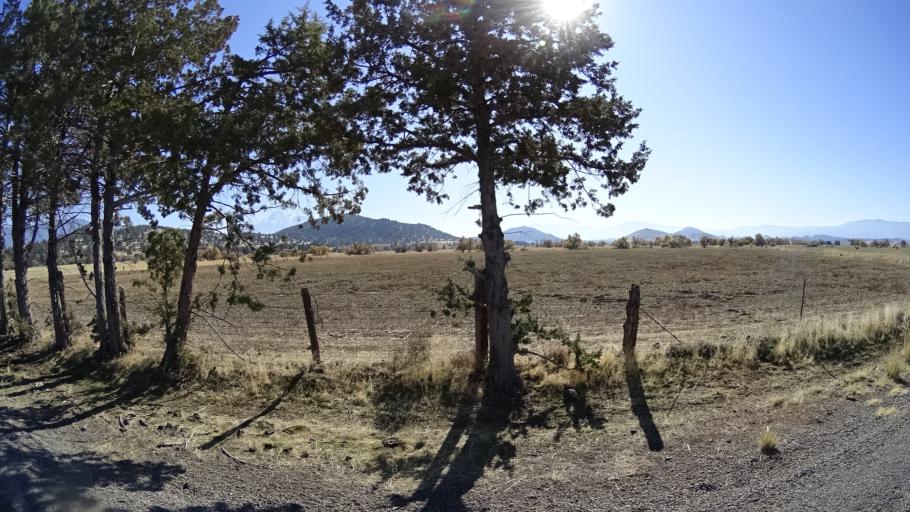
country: US
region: California
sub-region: Siskiyou County
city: Montague
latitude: 41.7263
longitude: -122.3763
